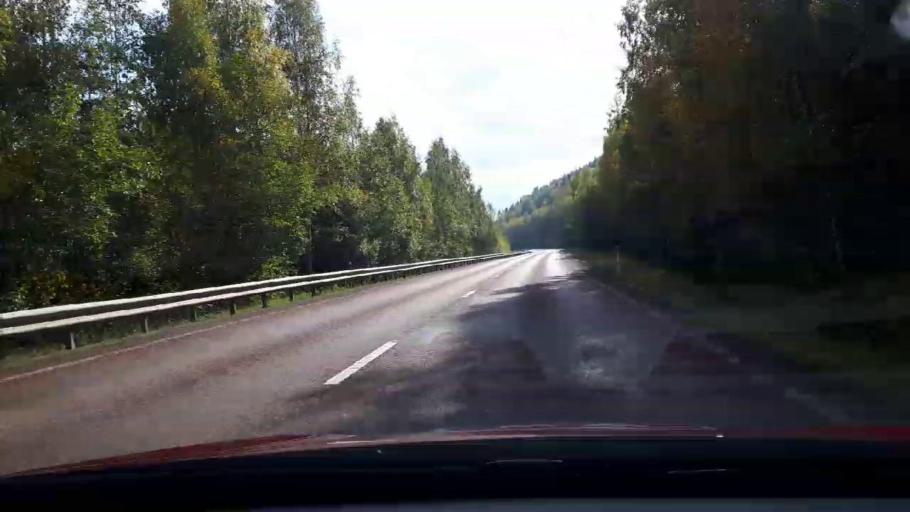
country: SE
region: Gaevleborg
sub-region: Ljusdals Kommun
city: Jaervsoe
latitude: 61.6311
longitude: 16.2761
